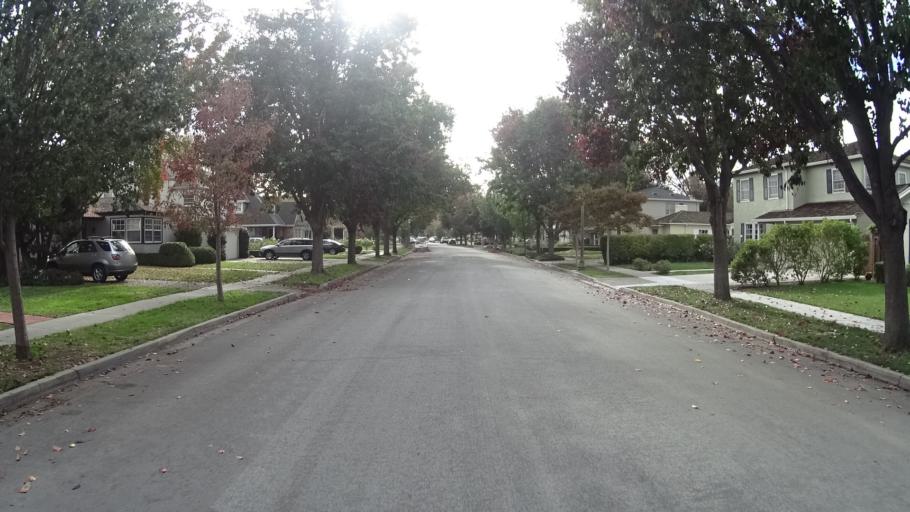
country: US
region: California
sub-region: Santa Clara County
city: Burbank
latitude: 37.3309
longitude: -121.9313
